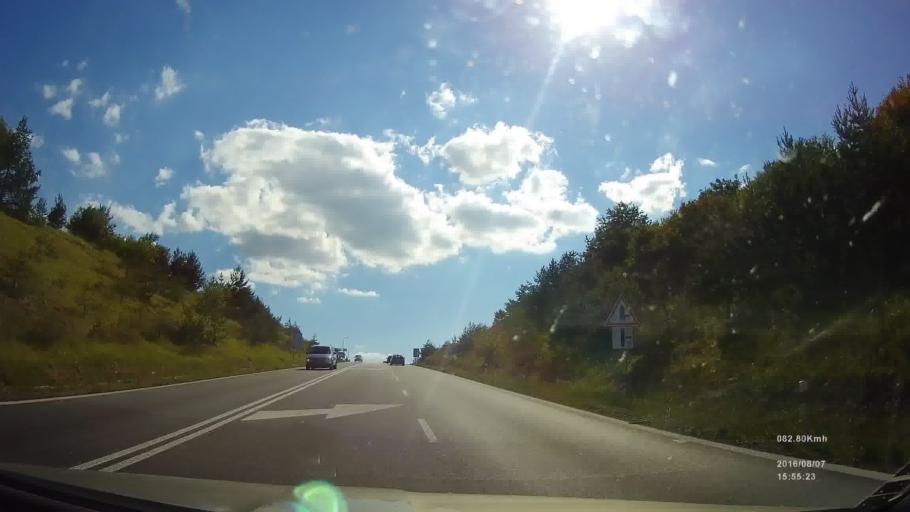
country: SK
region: Presovsky
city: Giraltovce
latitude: 49.0759
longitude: 21.4388
